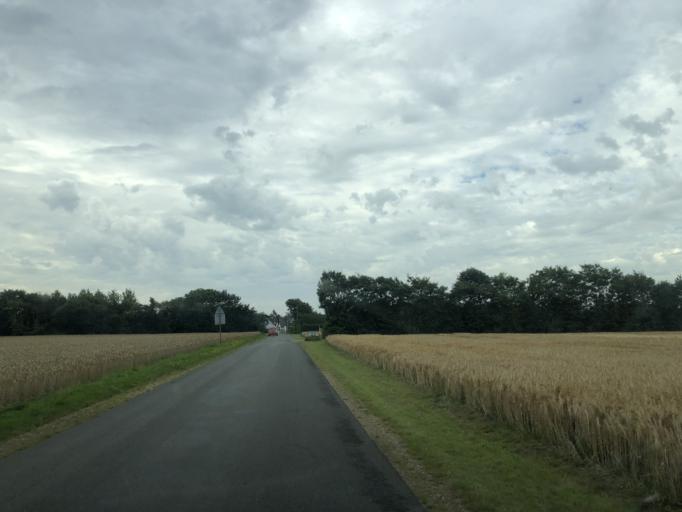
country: DK
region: Central Jutland
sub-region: Holstebro Kommune
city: Holstebro
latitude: 56.3788
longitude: 8.5230
